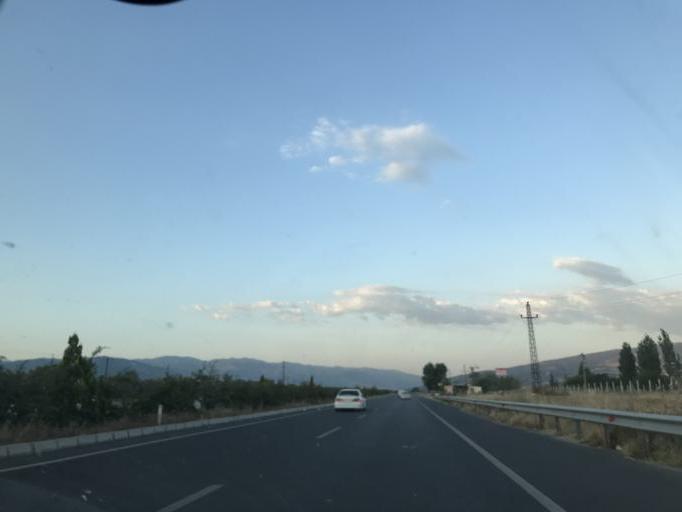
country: TR
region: Aydin
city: Horsunlu
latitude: 37.9193
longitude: 28.6315
